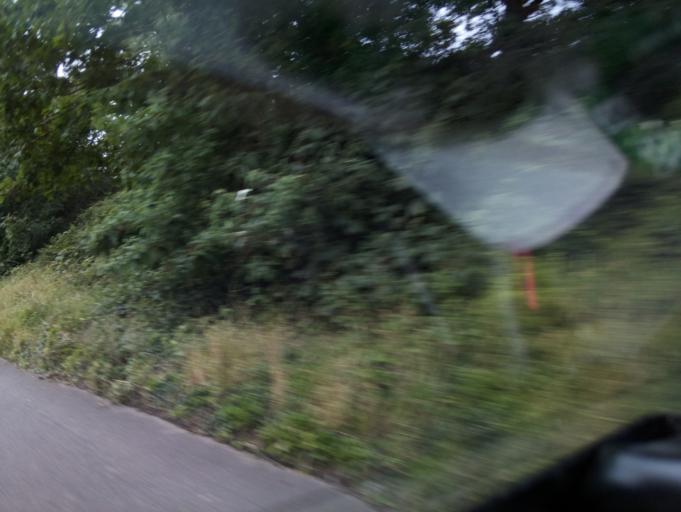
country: GB
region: England
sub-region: Devon
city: Kingsbridge
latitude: 50.2902
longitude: -3.7821
